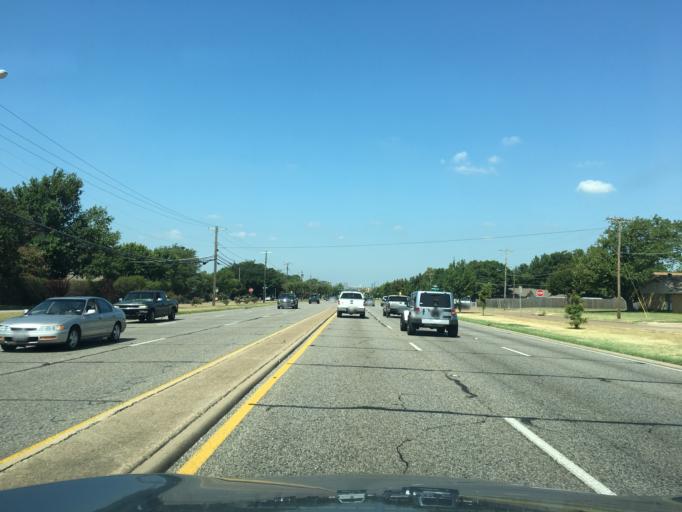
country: US
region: Texas
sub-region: Dallas County
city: Garland
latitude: 32.8642
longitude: -96.6880
